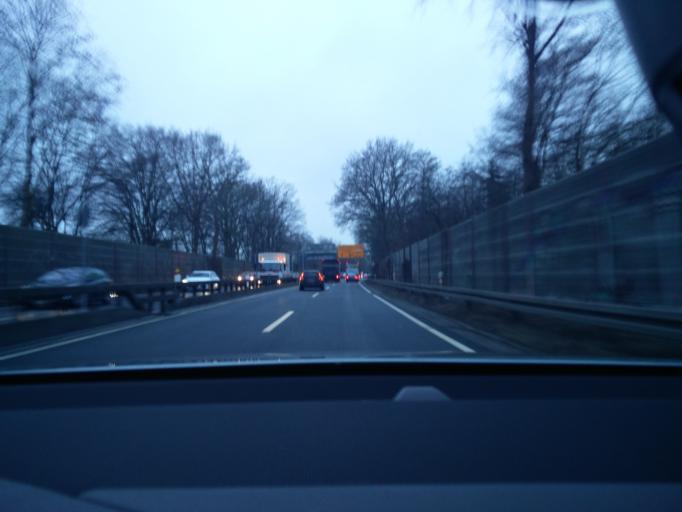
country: DE
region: Lower Saxony
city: Laatzen
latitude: 52.3468
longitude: 9.7854
